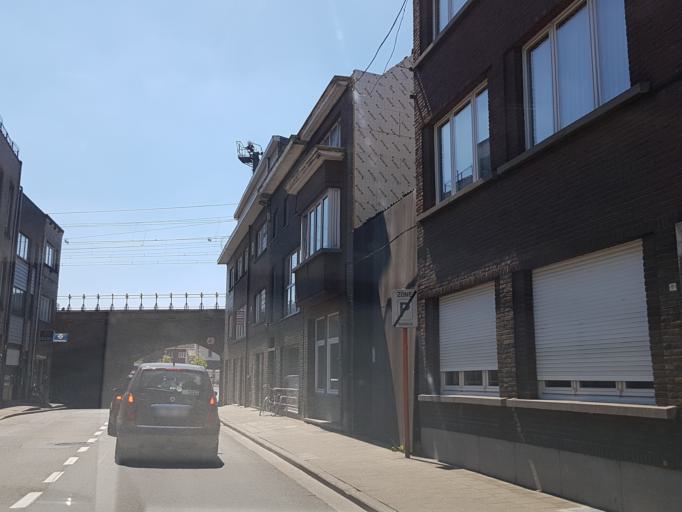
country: BE
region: Flanders
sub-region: Provincie Oost-Vlaanderen
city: Aalst
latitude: 50.9417
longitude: 4.0436
